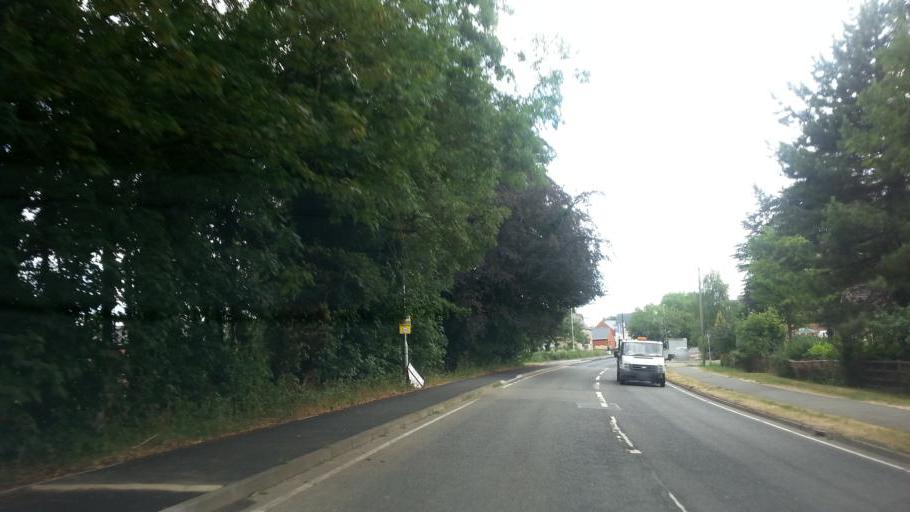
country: GB
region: England
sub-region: Northamptonshire
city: Silverstone
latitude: 52.0886
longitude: -1.0222
